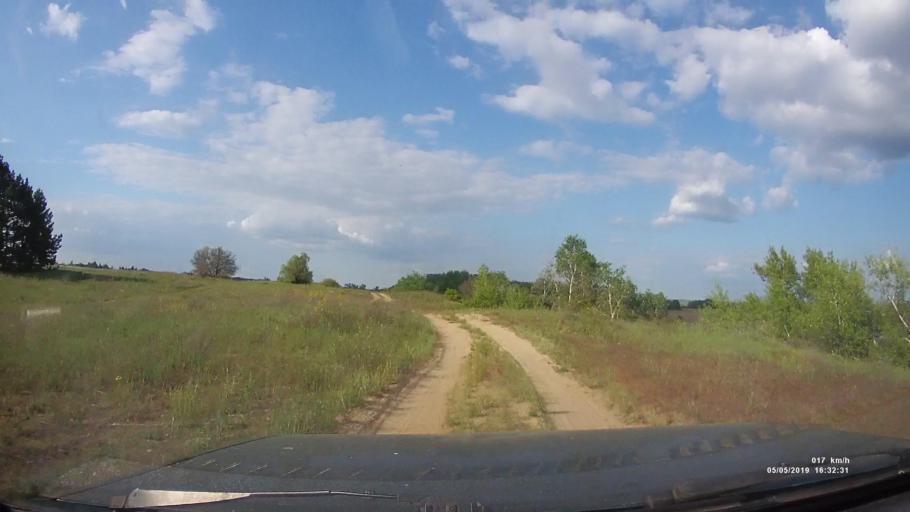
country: RU
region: Rostov
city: Ust'-Donetskiy
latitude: 47.7791
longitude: 41.0143
